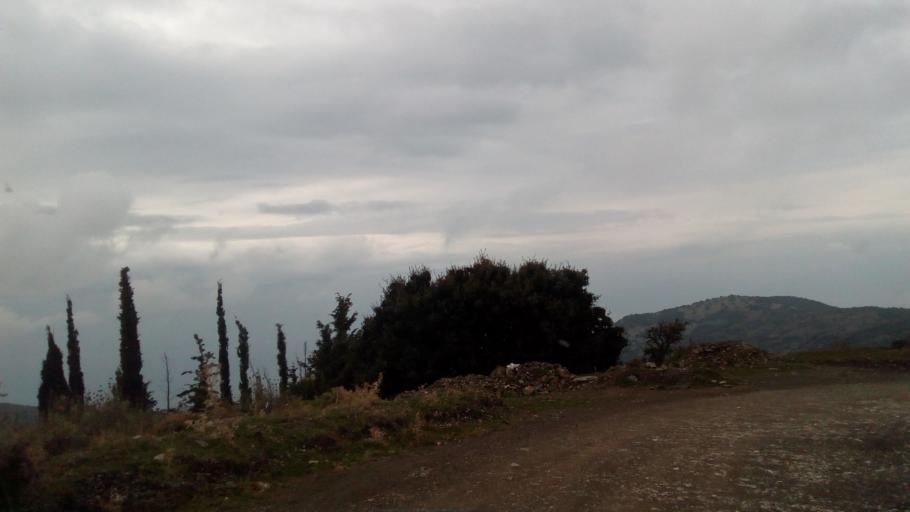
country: GR
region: Central Greece
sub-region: Nomos Fokidos
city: Lidoriki
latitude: 38.4185
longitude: 22.1056
